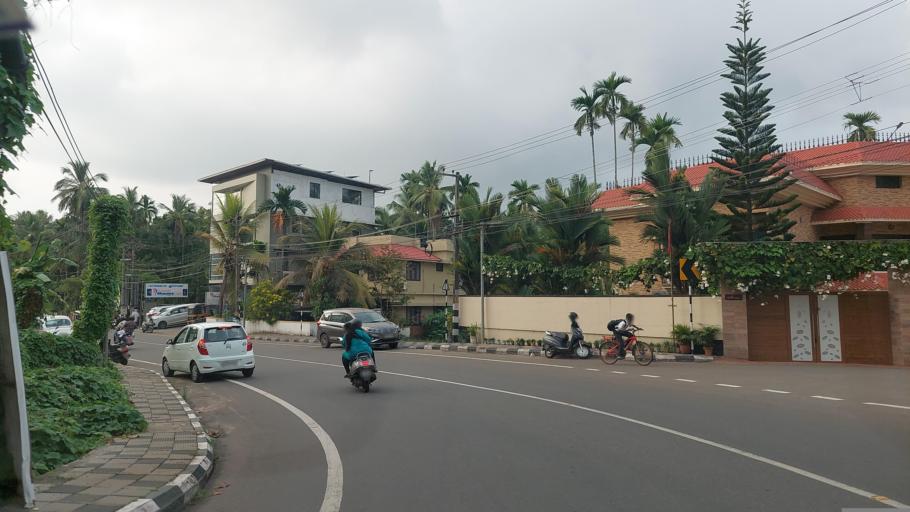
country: IN
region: Kerala
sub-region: Kozhikode
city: Kozhikode
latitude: 11.2919
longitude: 75.7671
